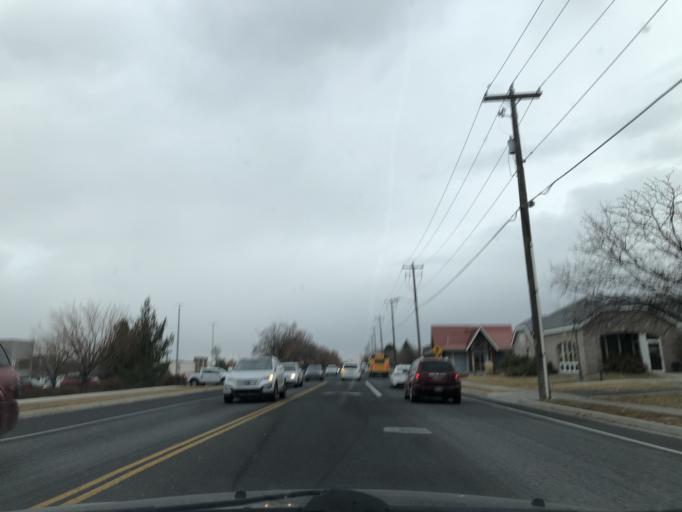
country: US
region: Utah
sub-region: Cache County
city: Logan
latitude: 41.7535
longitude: -111.8291
